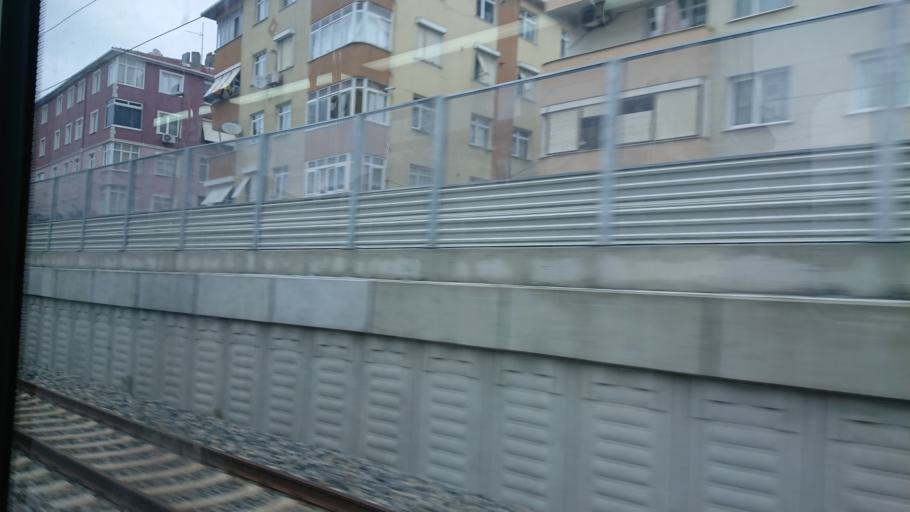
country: TR
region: Istanbul
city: Mahmutbey
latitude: 40.9967
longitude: 28.7673
